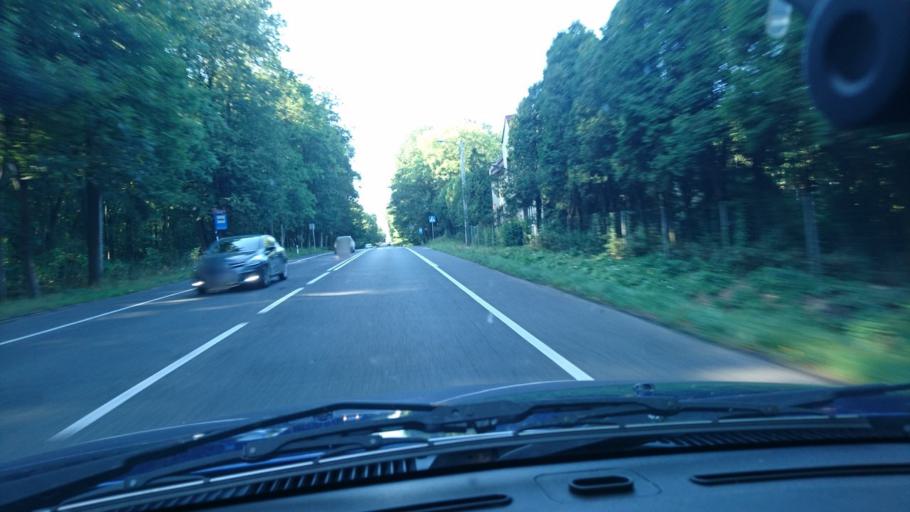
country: PL
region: Silesian Voivodeship
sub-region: Gliwice
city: Gliwice
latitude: 50.3427
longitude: 18.6514
